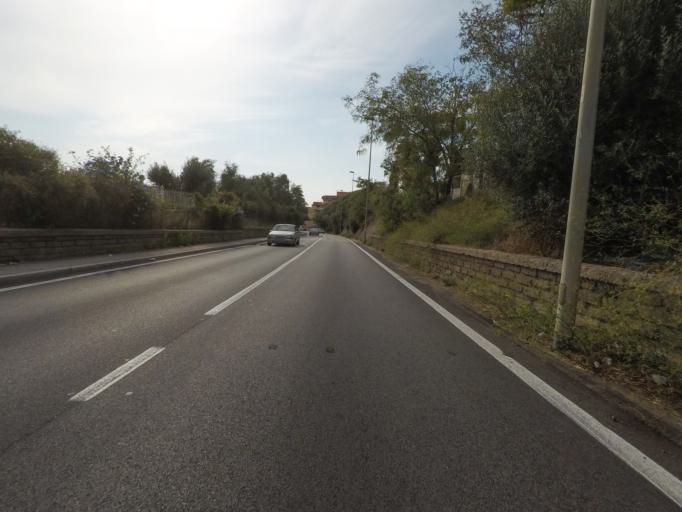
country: IT
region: Latium
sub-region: Citta metropolitana di Roma Capitale
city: Civitavecchia
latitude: 42.1015
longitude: 11.8039
